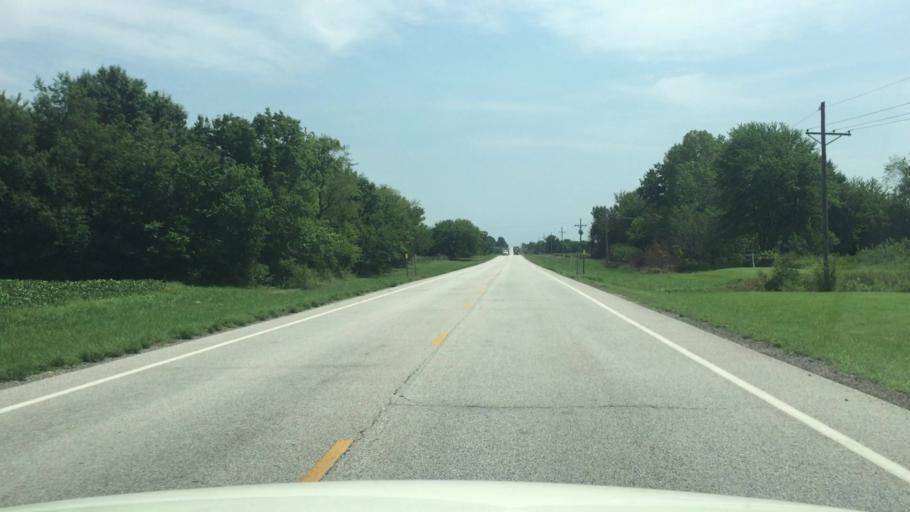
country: US
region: Kansas
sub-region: Cherokee County
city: Columbus
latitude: 37.1781
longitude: -94.8065
